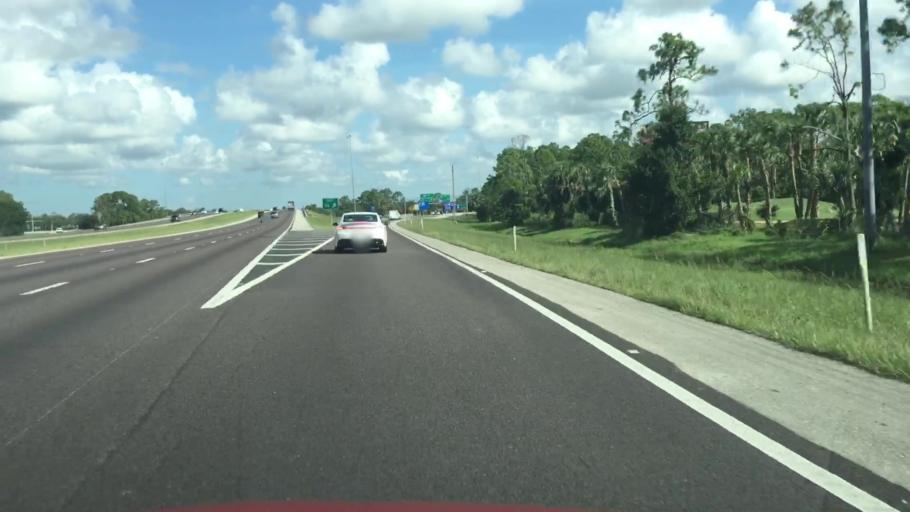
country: US
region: Florida
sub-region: Lee County
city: Bonita Springs
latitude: 26.3268
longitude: -81.7486
